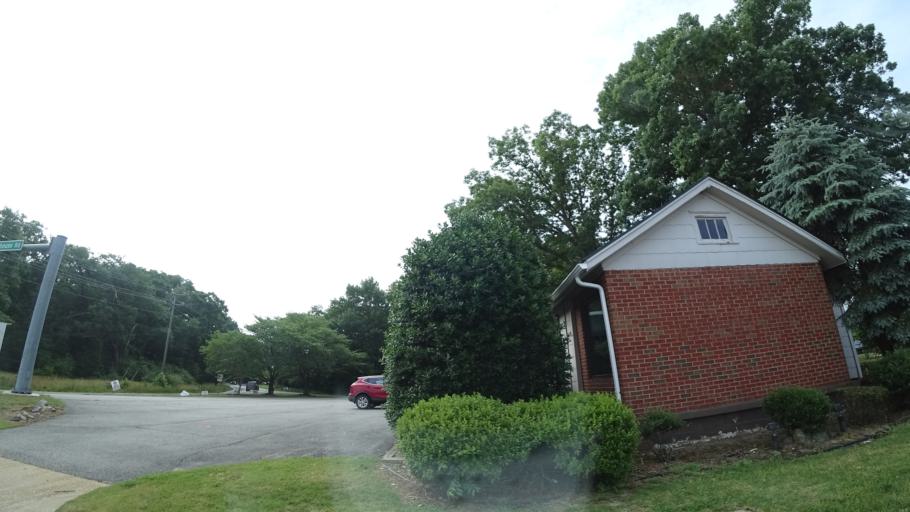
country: US
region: Virginia
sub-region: City of Fredericksburg
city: Fredericksburg
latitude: 38.2509
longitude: -77.5062
